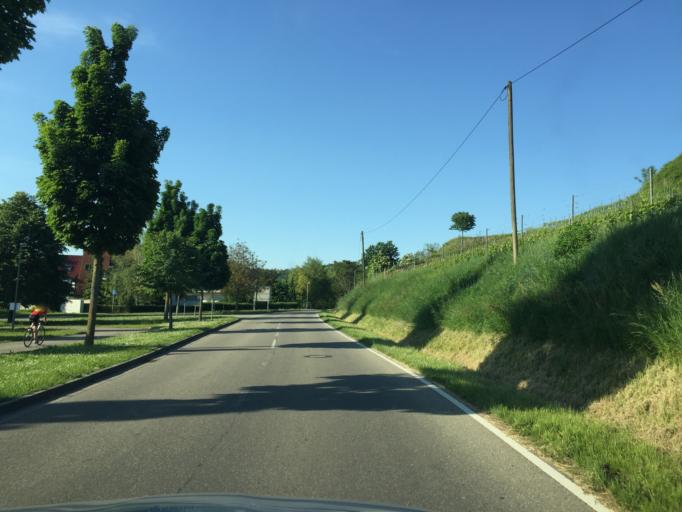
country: DE
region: Baden-Wuerttemberg
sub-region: Freiburg Region
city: Breisach am Rhein
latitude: 48.0596
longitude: 7.6089
